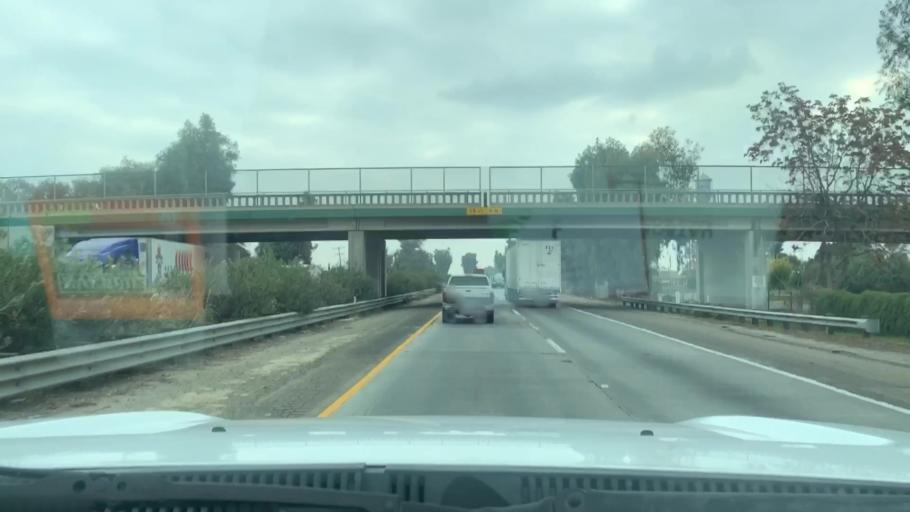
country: US
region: California
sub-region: Tulare County
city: Tipton
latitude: 36.0590
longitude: -119.3121
